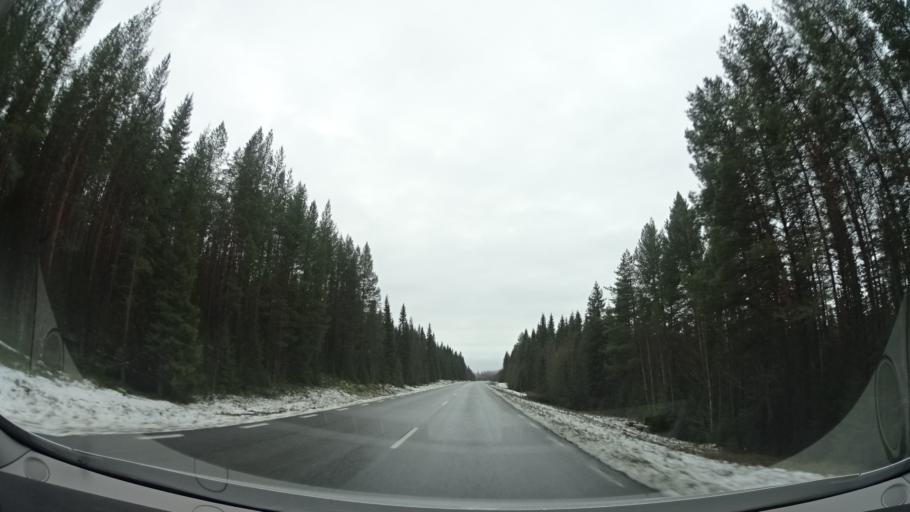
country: SE
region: Jaemtland
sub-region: Stroemsunds Kommun
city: Stroemsund
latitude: 64.0131
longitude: 15.5214
